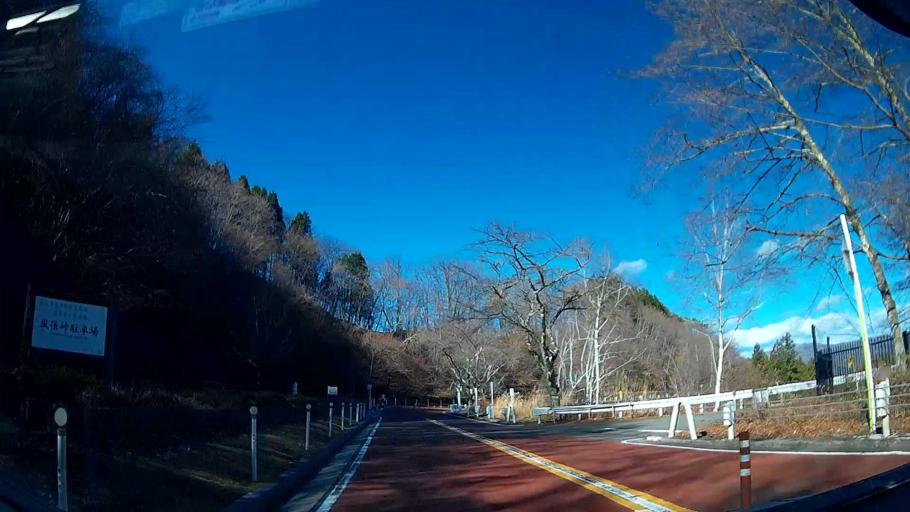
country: JP
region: Yamanashi
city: Uenohara
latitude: 35.7468
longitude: 139.0424
